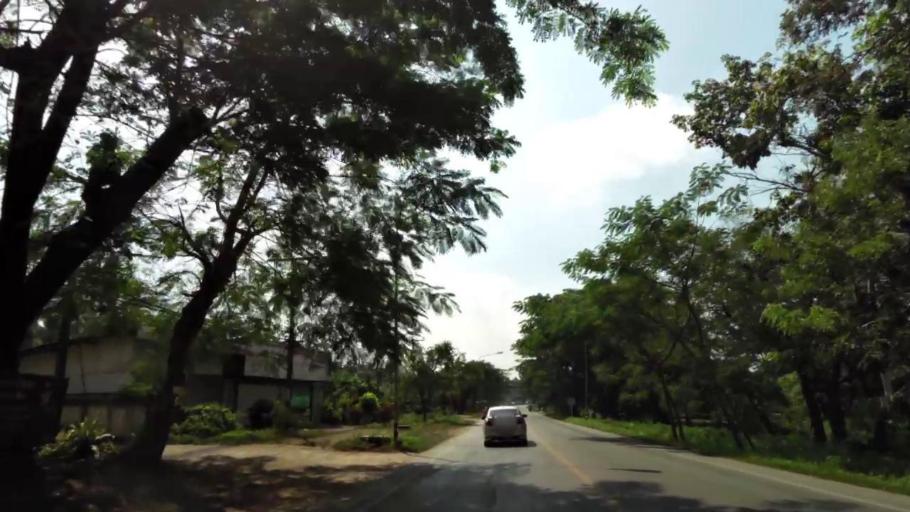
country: TH
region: Chiang Rai
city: Chiang Rai
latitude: 19.8744
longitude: 99.7820
